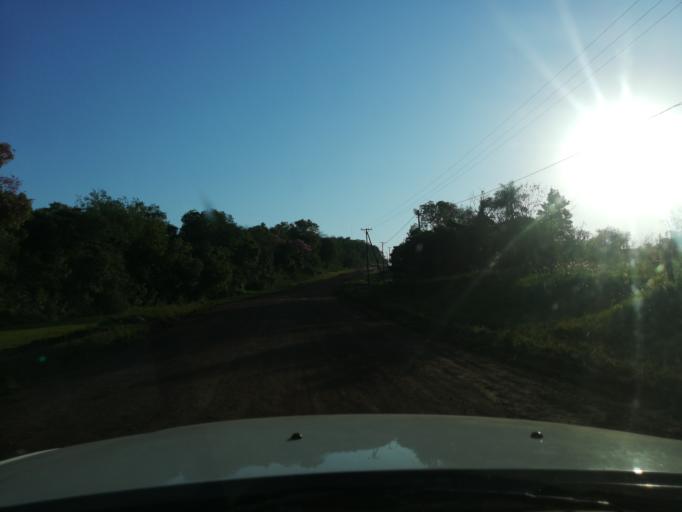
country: AR
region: Misiones
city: Cerro Cora
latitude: -27.6304
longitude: -55.7050
